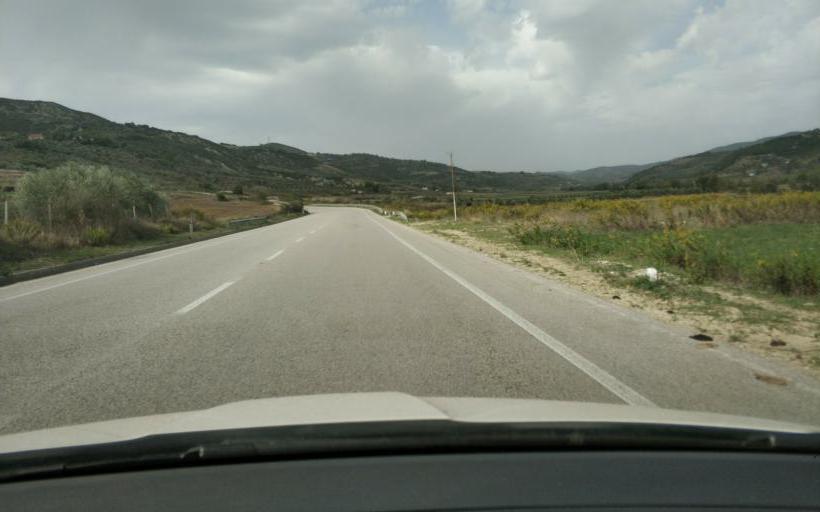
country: AL
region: Gjirokaster
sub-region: Rrethi i Tepelenes
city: Krahes
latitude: 40.4369
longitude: 19.8507
